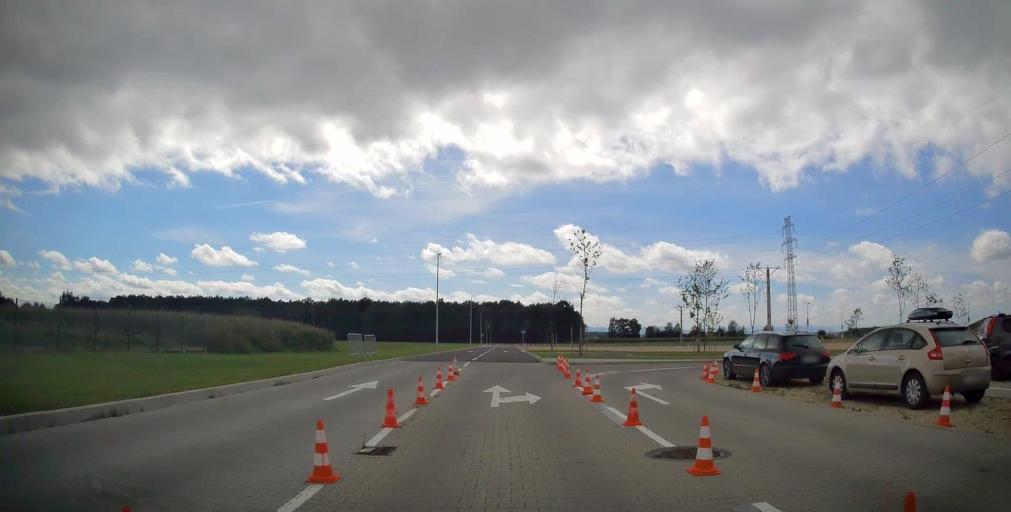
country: PL
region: Lesser Poland Voivodeship
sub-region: Powiat oswiecimski
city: Zator
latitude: 49.9943
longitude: 19.4145
